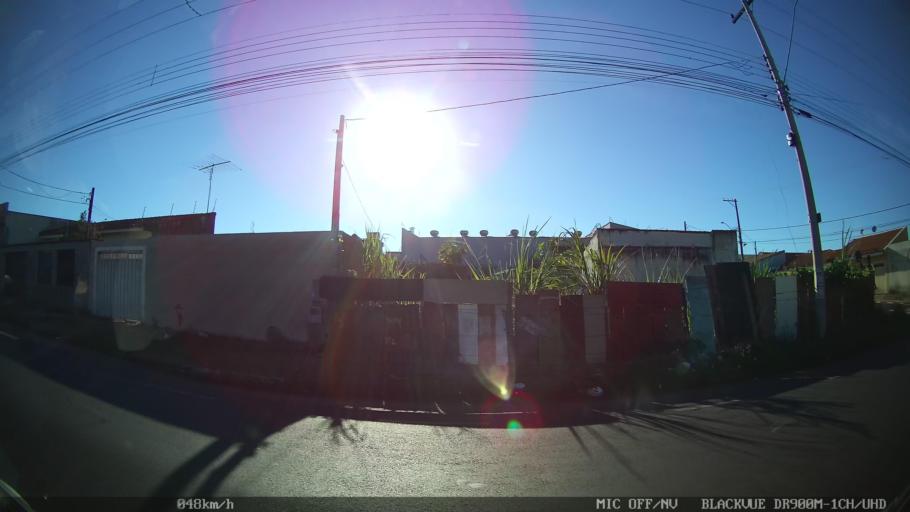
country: BR
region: Sao Paulo
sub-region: Franca
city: Franca
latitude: -20.5805
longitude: -47.3850
